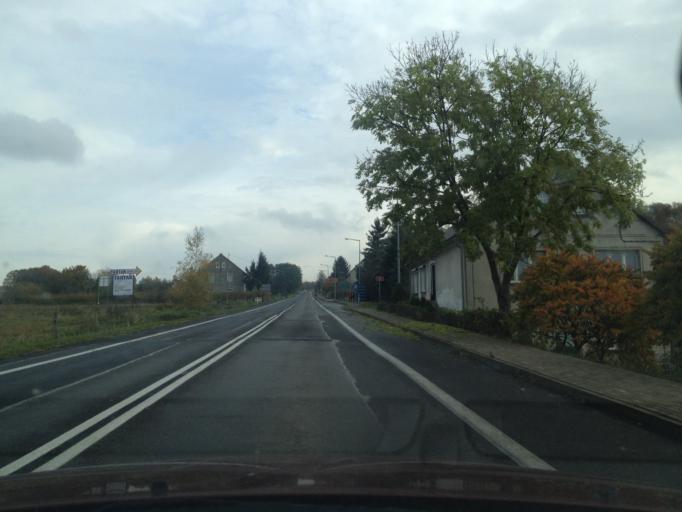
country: PL
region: Lower Silesian Voivodeship
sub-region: Powiat zgorzelecki
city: Lagow
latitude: 51.1561
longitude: 15.1223
